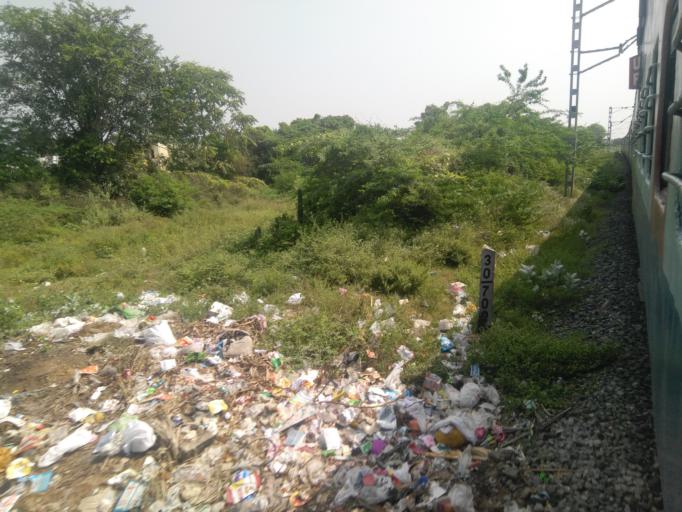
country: IN
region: Tamil Nadu
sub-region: Coimbatore
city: Mettupalayam
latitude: 11.2805
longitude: 76.9407
